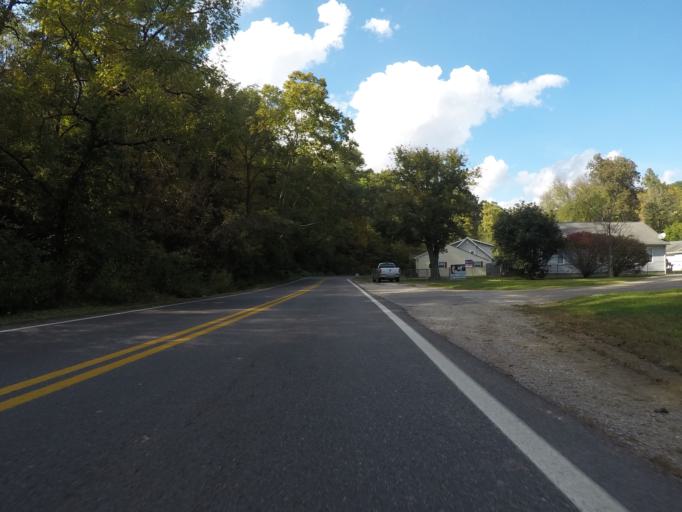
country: US
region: Ohio
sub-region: Lawrence County
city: Burlington
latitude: 38.3886
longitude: -82.5117
